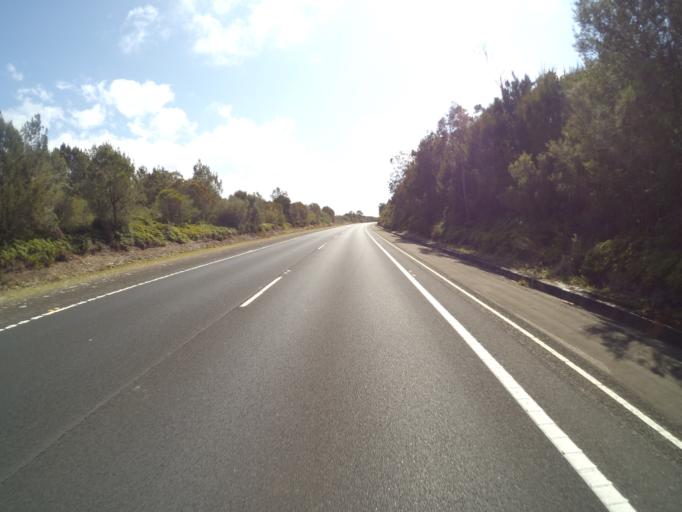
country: AU
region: New South Wales
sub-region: Wollongong
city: Bulli
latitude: -34.2694
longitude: 150.9271
